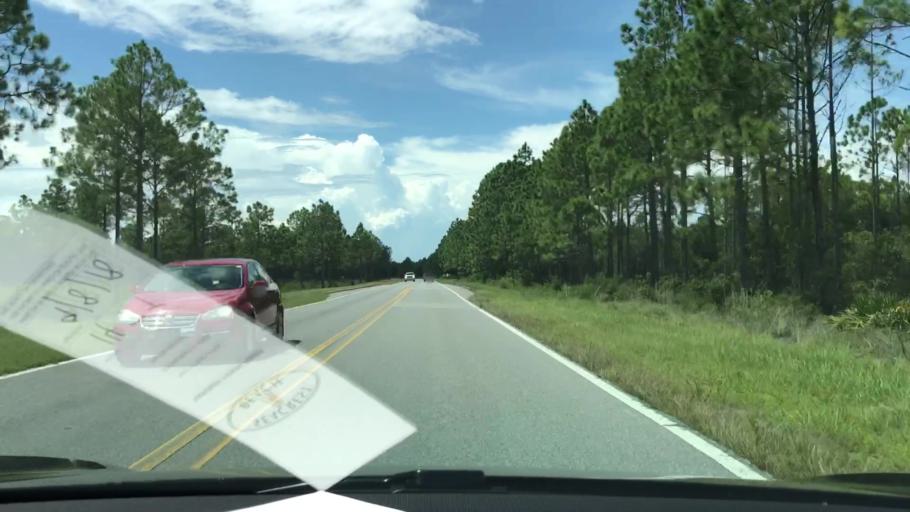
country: US
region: Florida
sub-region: Walton County
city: Seaside
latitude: 30.2944
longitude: -86.0306
